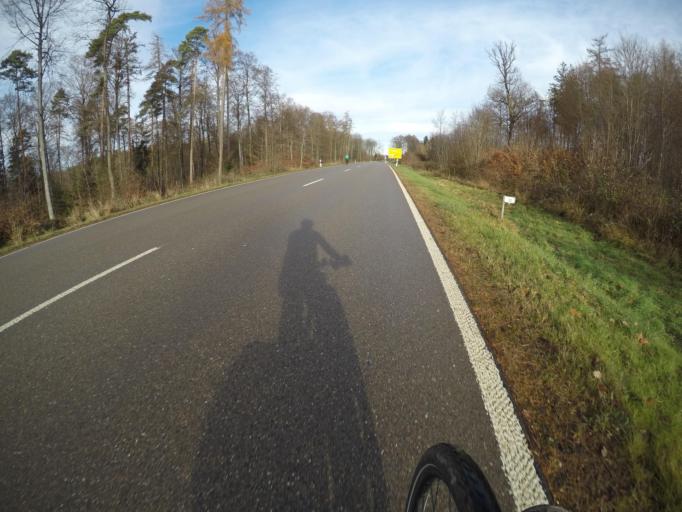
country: DE
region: Baden-Wuerttemberg
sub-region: Regierungsbezirk Stuttgart
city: Winterbach
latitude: 48.7745
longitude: 9.4594
